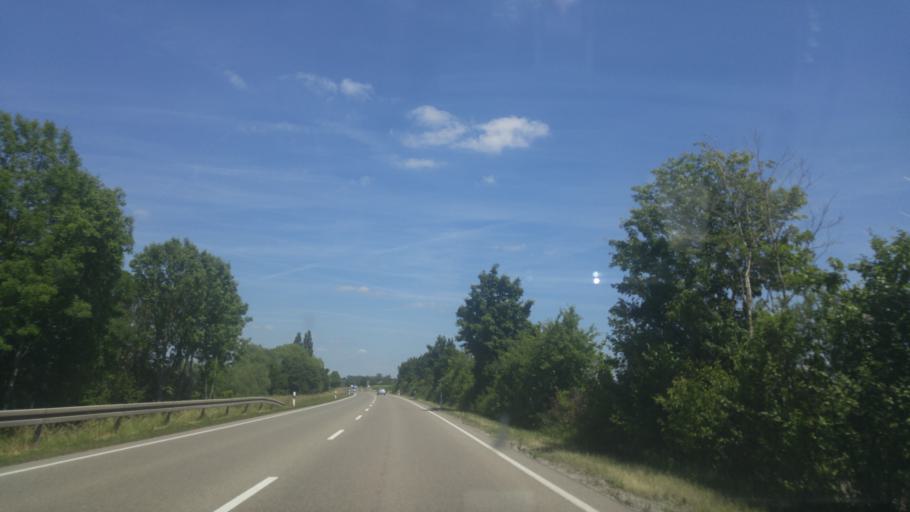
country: DE
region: Bavaria
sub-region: Regierungsbezirk Mittelfranken
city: Illesheim
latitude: 49.4710
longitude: 10.3621
